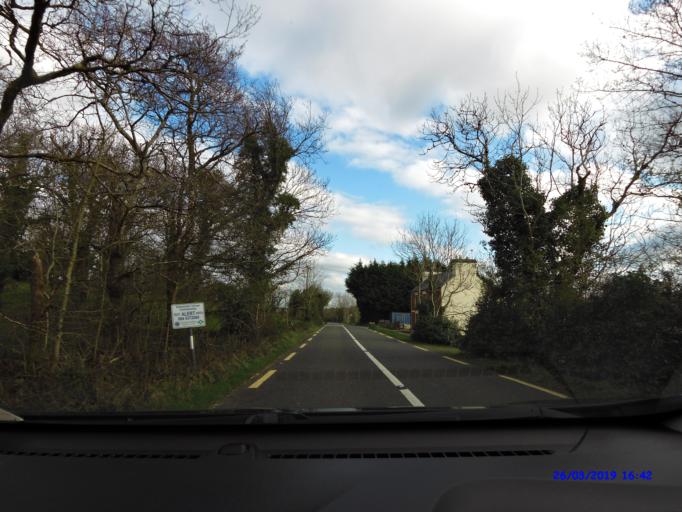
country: IE
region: Connaught
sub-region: Maigh Eo
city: Ballyhaunis
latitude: 53.8671
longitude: -8.7659
